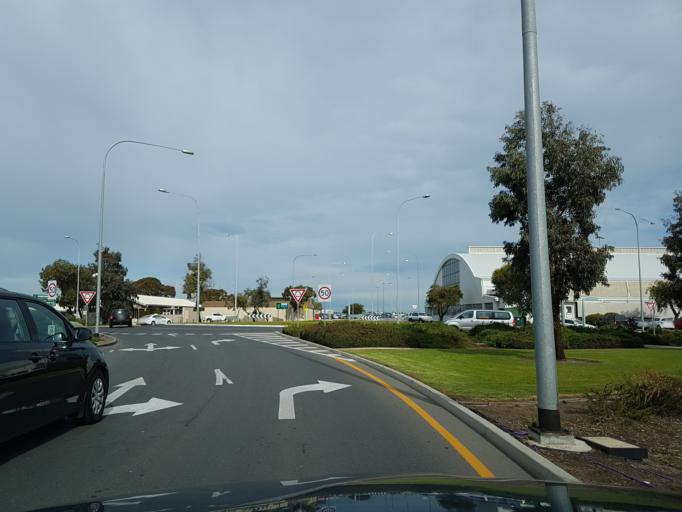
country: AU
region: South Australia
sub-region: City of West Torrens
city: Plympton
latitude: -34.9390
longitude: 138.5348
